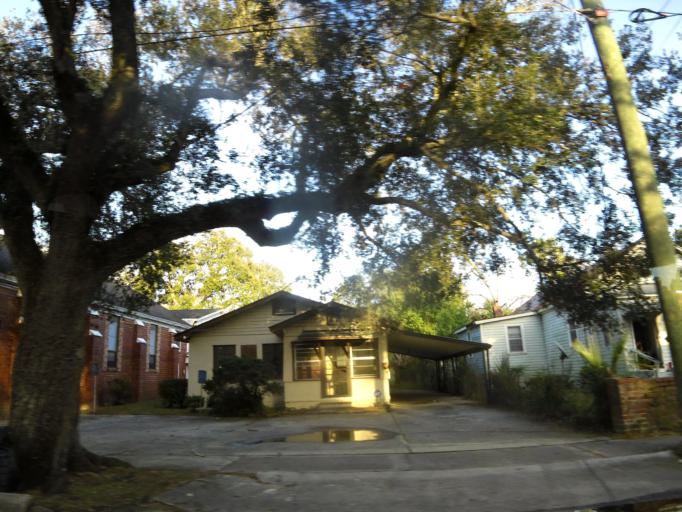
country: US
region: Florida
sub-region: Duval County
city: Jacksonville
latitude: 30.3398
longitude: -81.6403
